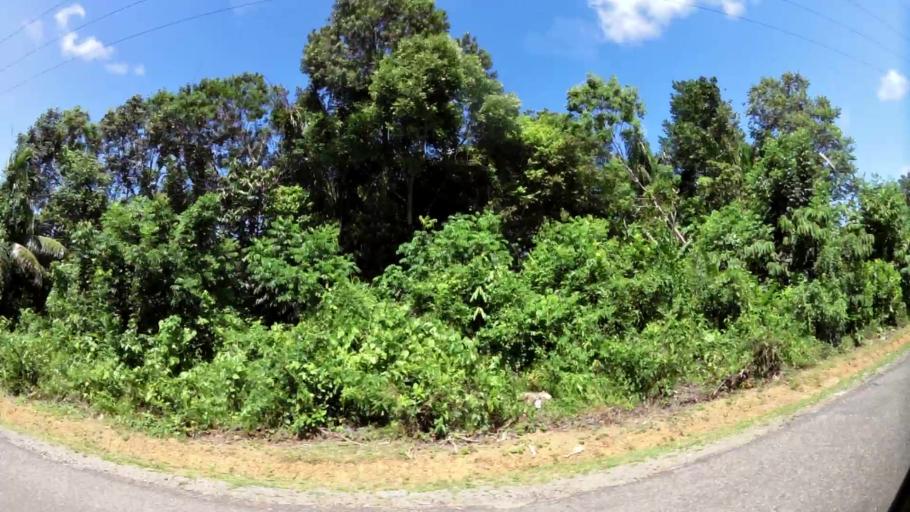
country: GF
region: Guyane
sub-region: Guyane
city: Matoury
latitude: 4.8361
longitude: -52.3267
